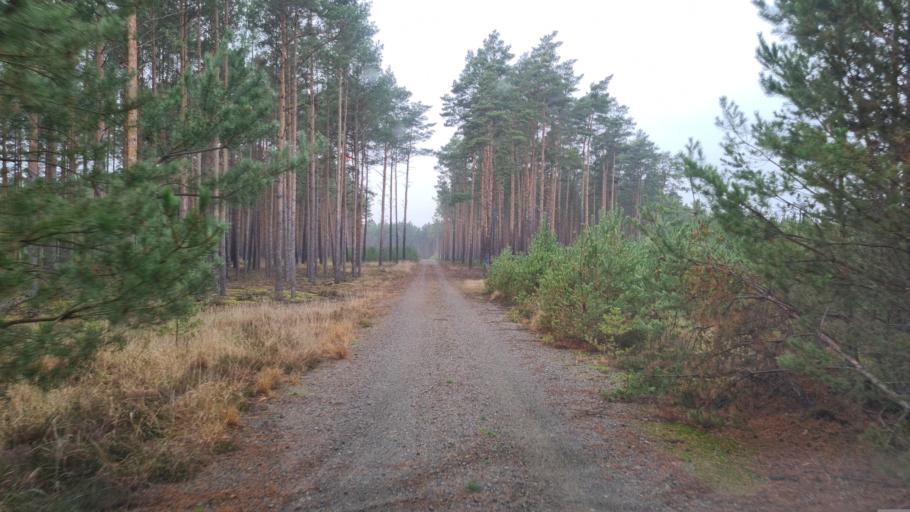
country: DE
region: Brandenburg
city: Sallgast
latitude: 51.6456
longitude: 13.8218
